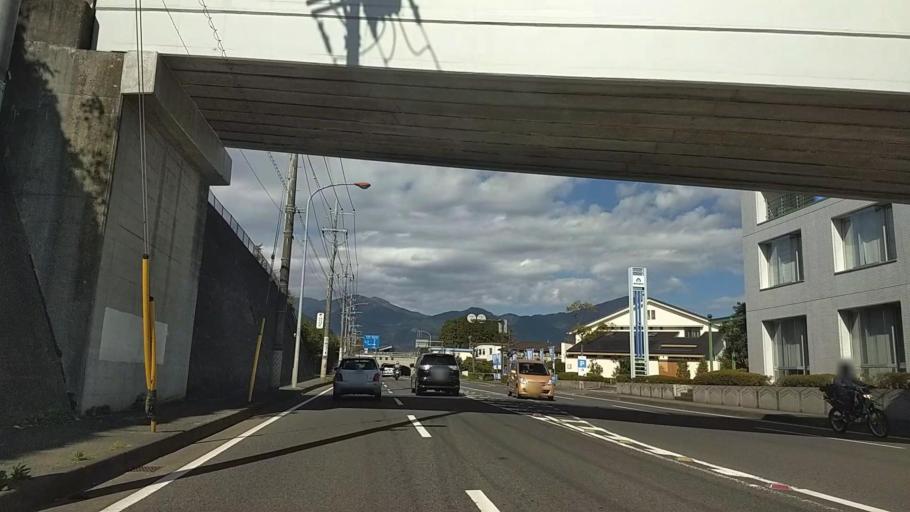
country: JP
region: Kanagawa
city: Hadano
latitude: 35.3579
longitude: 139.2350
